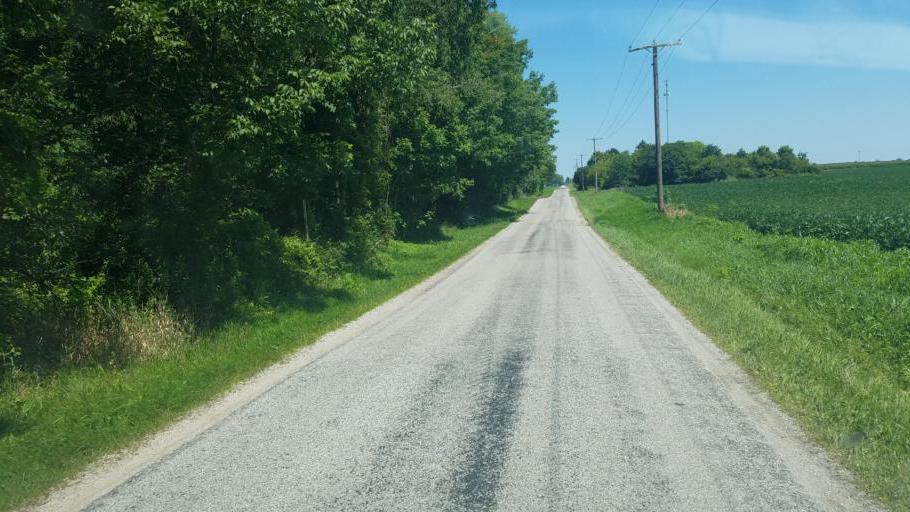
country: US
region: Ohio
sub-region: Delaware County
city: Ashley
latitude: 40.4540
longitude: -83.0485
